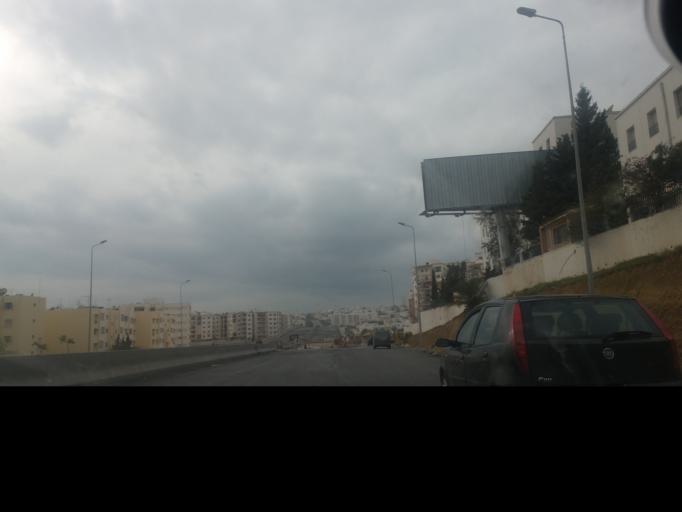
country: TN
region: Tunis
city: Tunis
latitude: 36.8550
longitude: 10.1564
